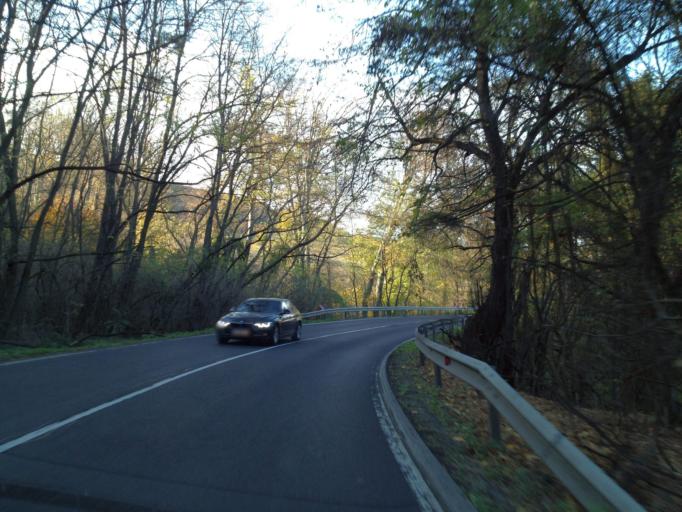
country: HU
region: Gyor-Moson-Sopron
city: Bakonyszentlaszlo
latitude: 47.3555
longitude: 17.8718
